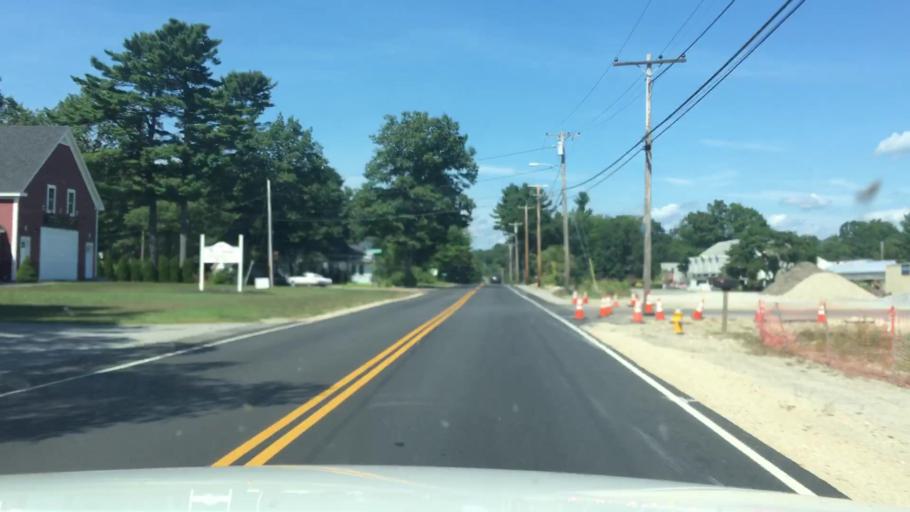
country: US
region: Maine
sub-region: Cumberland County
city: Cumberland Center
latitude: 43.8173
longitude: -70.3141
